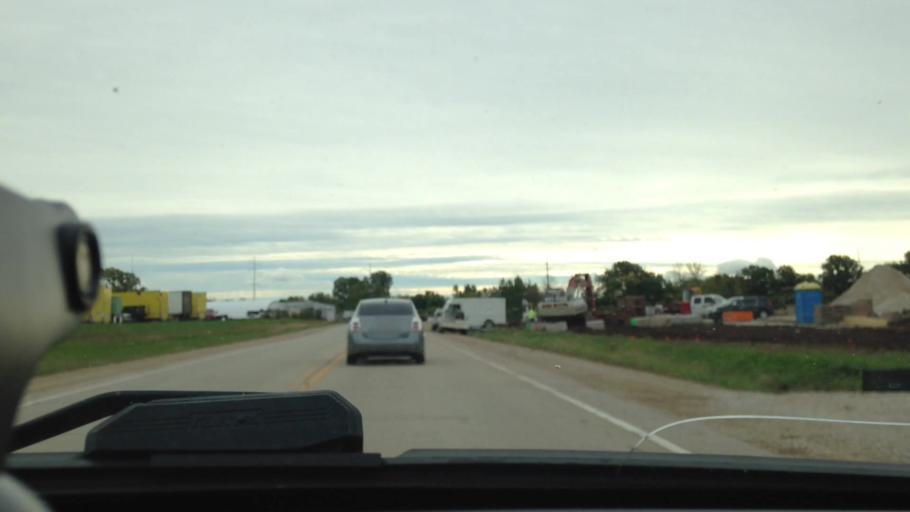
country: US
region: Wisconsin
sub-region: Fond du Lac County
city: North Fond du Lac
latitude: 43.7977
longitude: -88.4903
